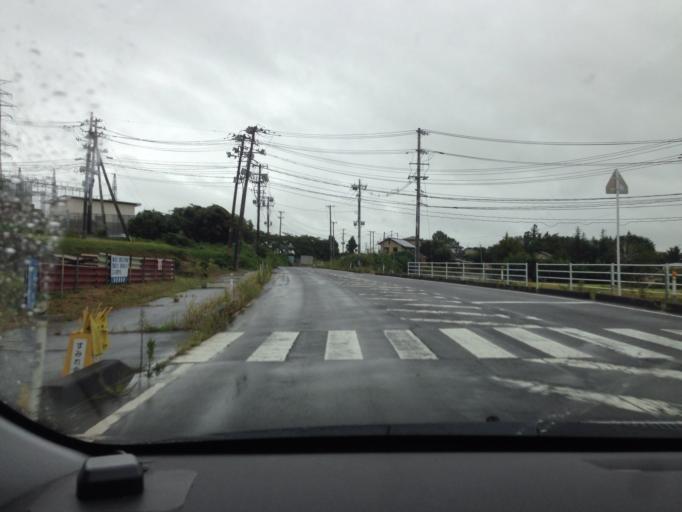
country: JP
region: Fukushima
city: Koriyama
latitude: 37.4560
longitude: 140.3280
